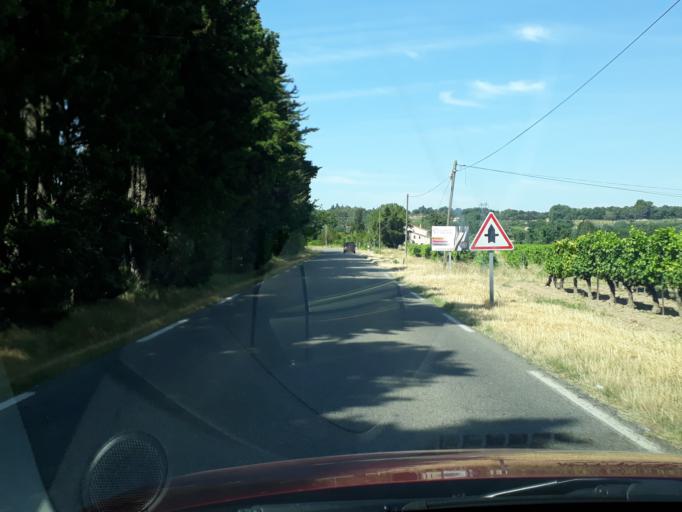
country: FR
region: Provence-Alpes-Cote d'Azur
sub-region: Departement du Vaucluse
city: Vacqueyras
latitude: 44.1110
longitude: 4.9885
